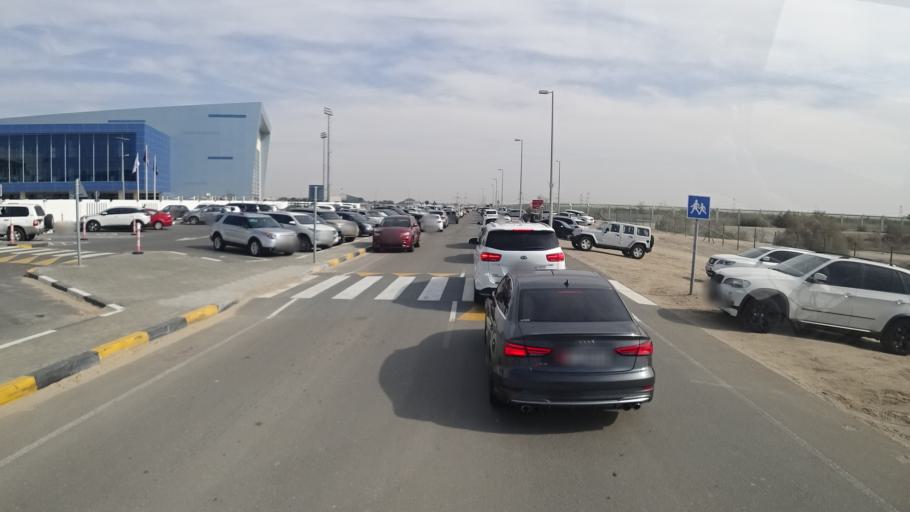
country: AE
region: Abu Dhabi
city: Abu Dhabi
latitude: 24.5366
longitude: 54.6304
